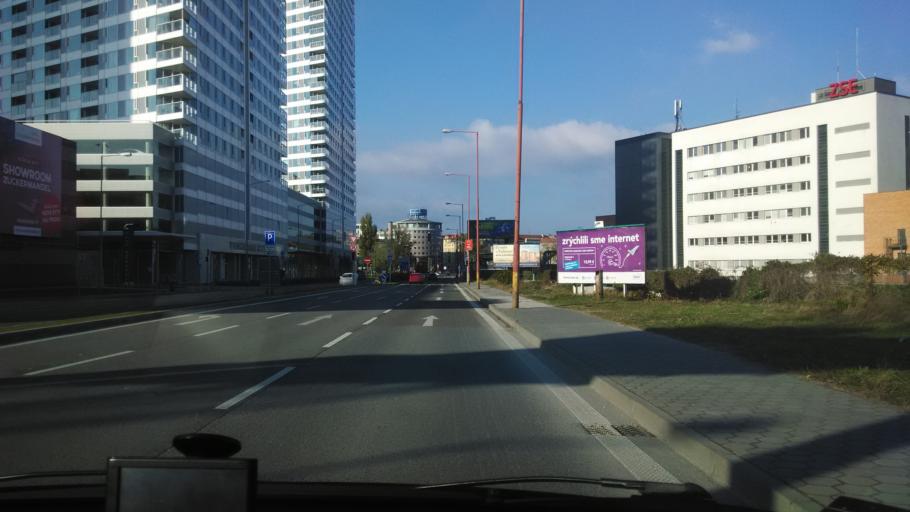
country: SK
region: Bratislavsky
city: Bratislava
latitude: 48.1424
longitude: 17.1280
